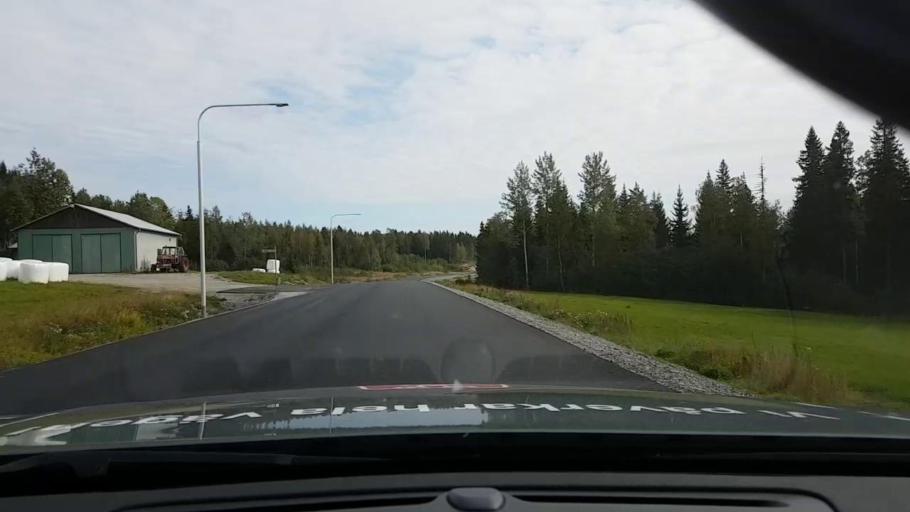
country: SE
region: Vaesternorrland
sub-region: OErnskoeldsviks Kommun
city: Bjasta
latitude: 63.2928
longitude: 18.4940
